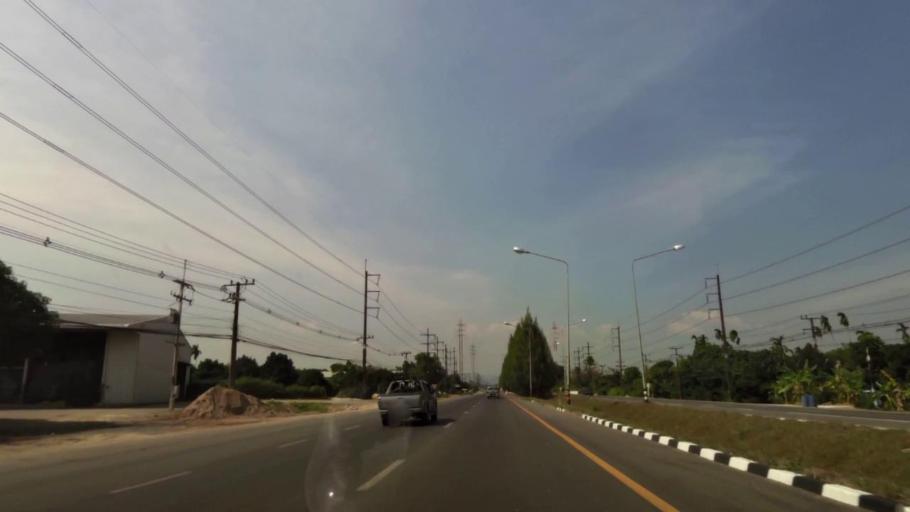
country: TH
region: Chanthaburi
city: Chanthaburi
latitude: 12.6344
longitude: 102.1402
